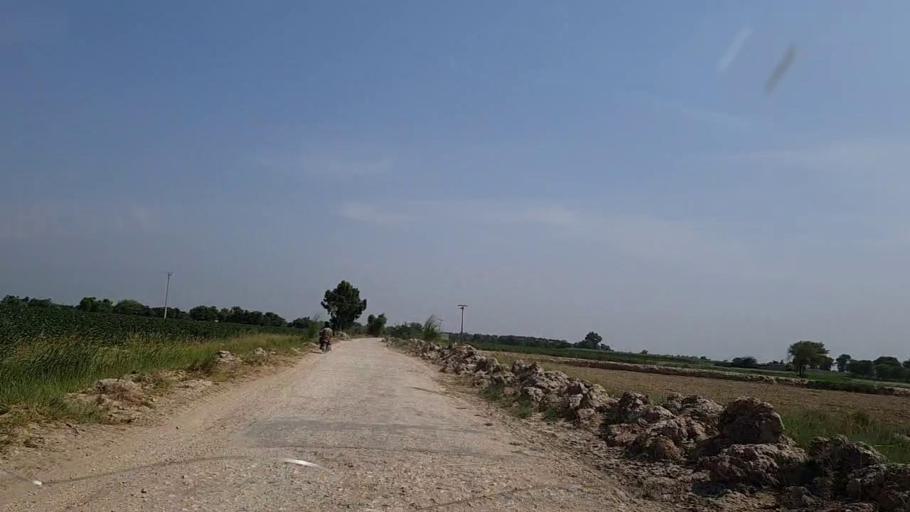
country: PK
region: Sindh
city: Khanpur
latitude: 27.7911
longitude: 69.3172
